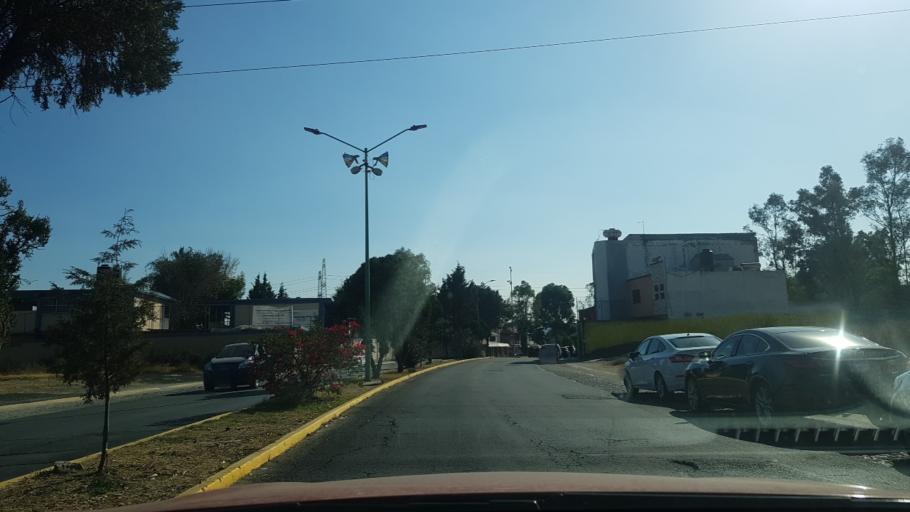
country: MX
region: Mexico
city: Cuautitlan Izcalli
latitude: 19.6392
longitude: -99.1996
